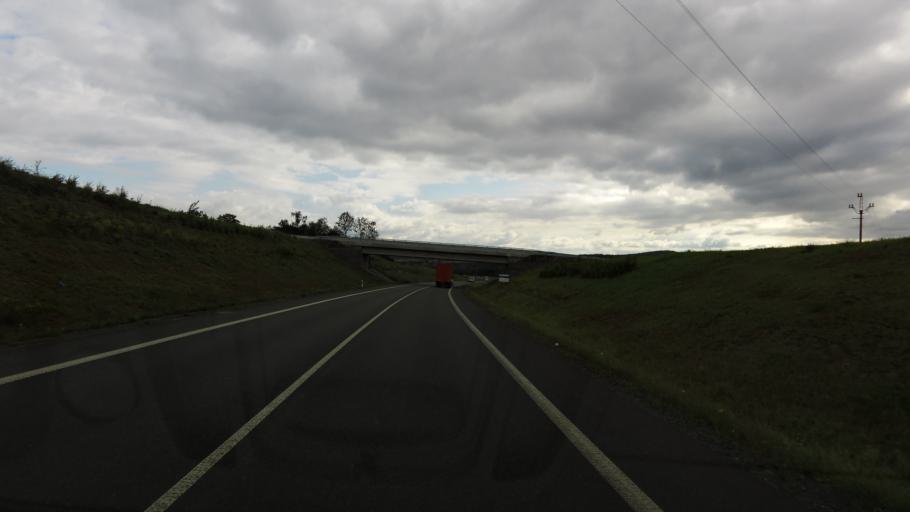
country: CZ
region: Plzensky
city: Stankov
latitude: 49.5610
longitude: 13.0653
